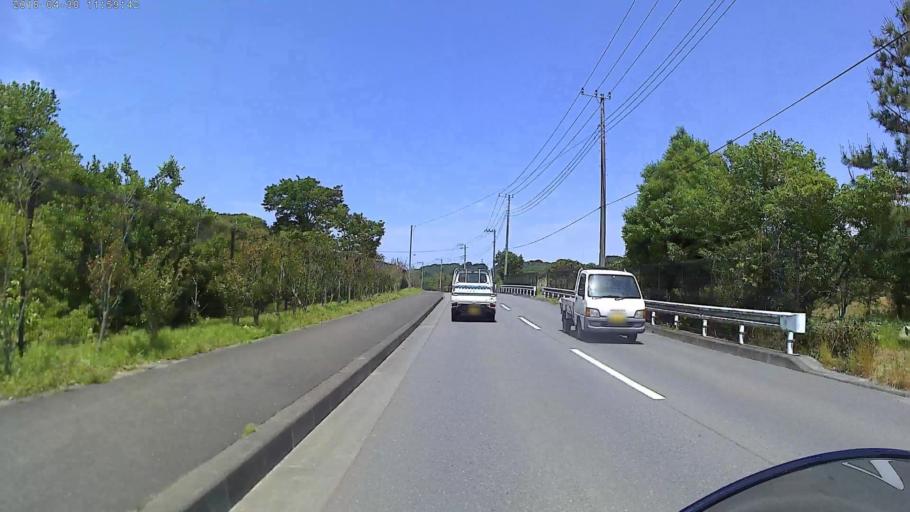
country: JP
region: Kanagawa
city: Zama
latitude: 35.5094
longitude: 139.3286
